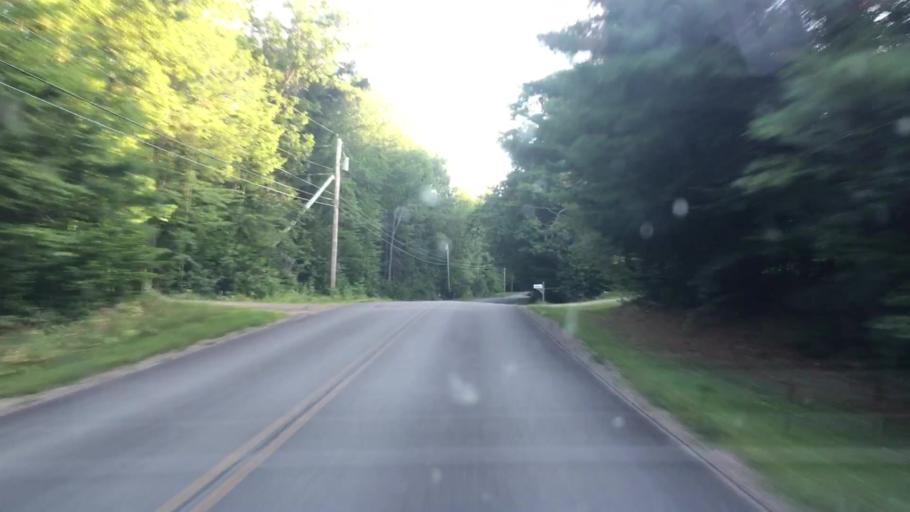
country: US
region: Maine
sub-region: Penobscot County
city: Hampden
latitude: 44.6989
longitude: -68.8951
